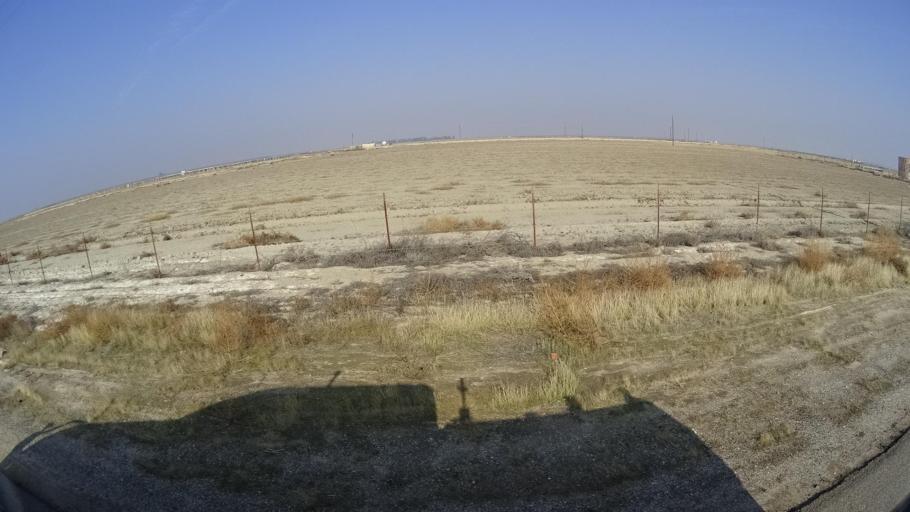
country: US
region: California
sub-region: Kern County
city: Buttonwillow
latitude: 35.3331
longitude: -119.3660
